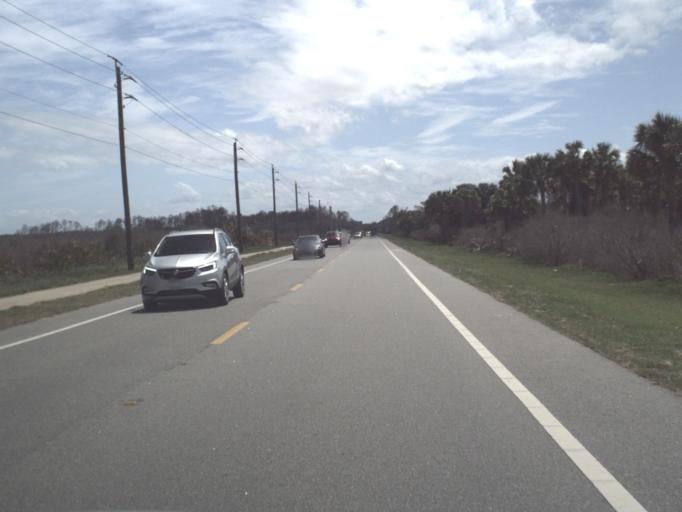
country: US
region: Florida
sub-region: Flagler County
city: Palm Coast
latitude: 29.6395
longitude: -81.2039
